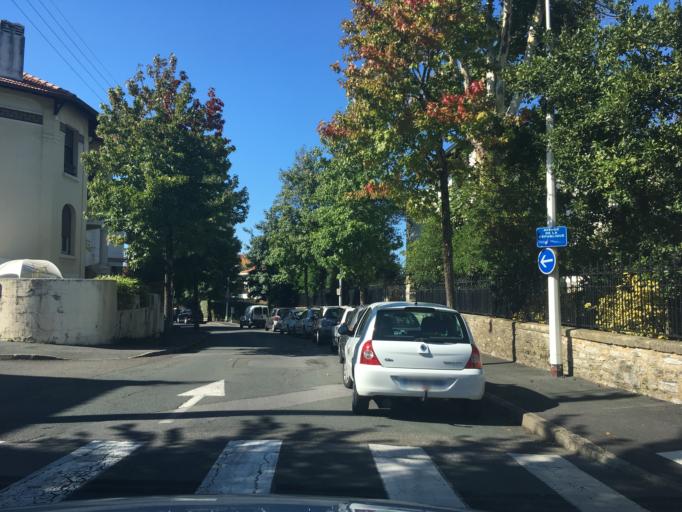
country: FR
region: Aquitaine
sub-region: Departement des Pyrenees-Atlantiques
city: Biarritz
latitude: 43.4753
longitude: -1.5577
